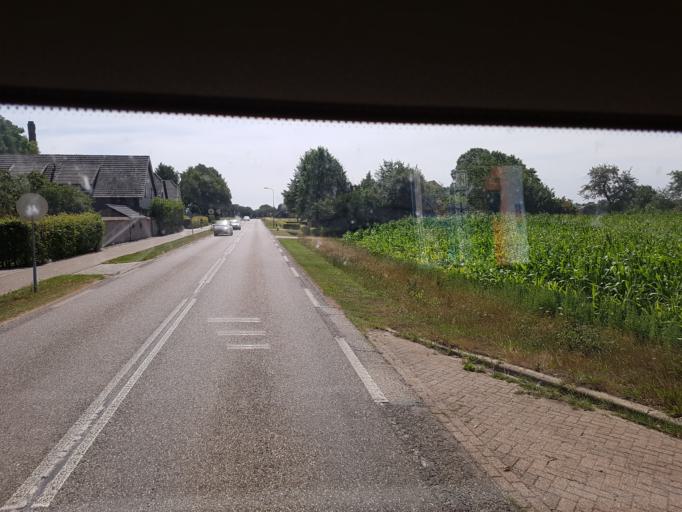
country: NL
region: Limburg
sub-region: Gemeente Leudal
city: Kelpen-Oler
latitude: 51.2065
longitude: 5.8046
